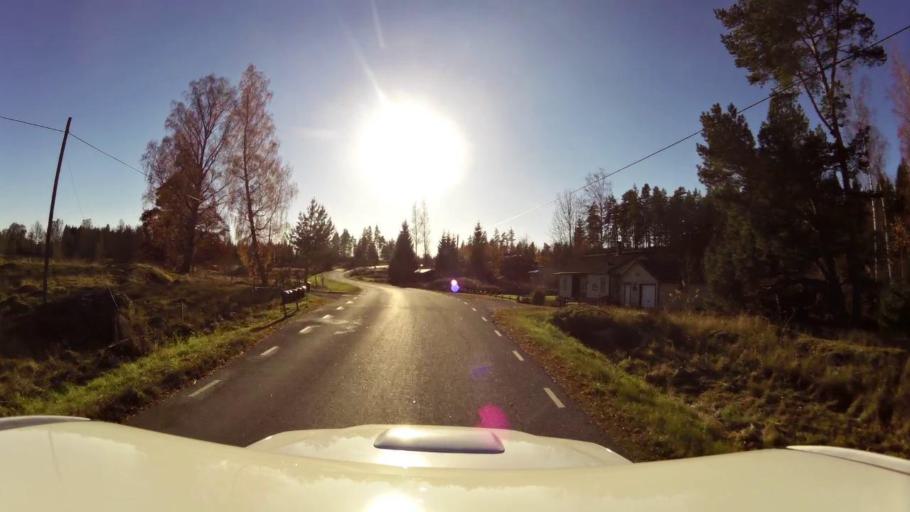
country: SE
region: OEstergoetland
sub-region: Linkopings Kommun
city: Sturefors
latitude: 58.2802
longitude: 15.6560
